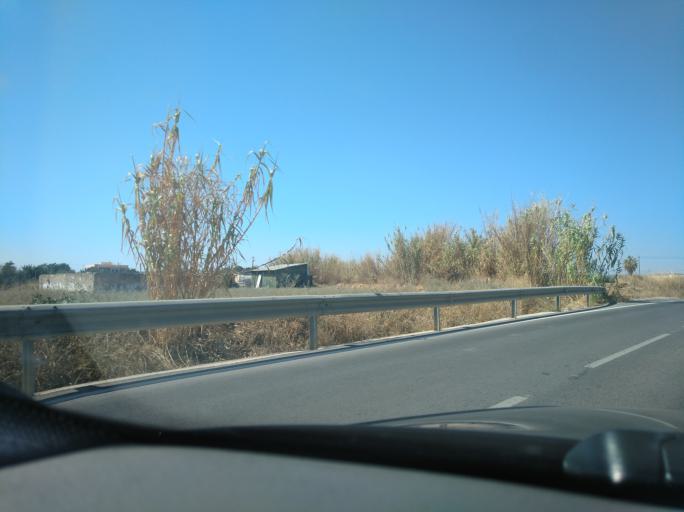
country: PT
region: Faro
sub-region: Faro
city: Faro
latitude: 37.0288
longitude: -7.8976
